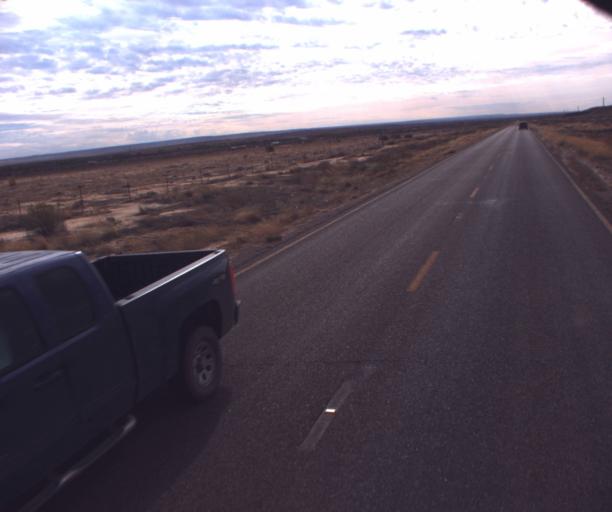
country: US
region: Arizona
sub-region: Apache County
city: Many Farms
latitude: 36.3177
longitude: -109.6147
